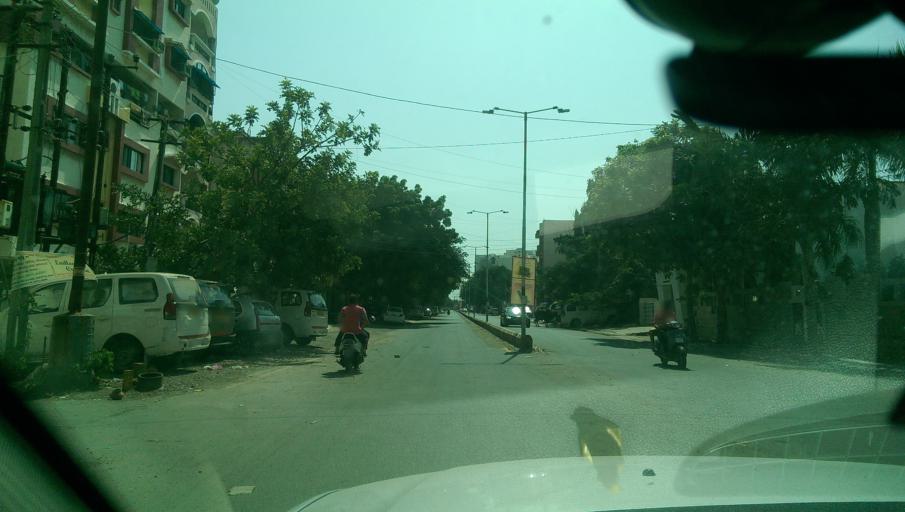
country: IN
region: Gujarat
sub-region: Jamnagar
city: Jamnagar
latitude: 22.4832
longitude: 70.0551
